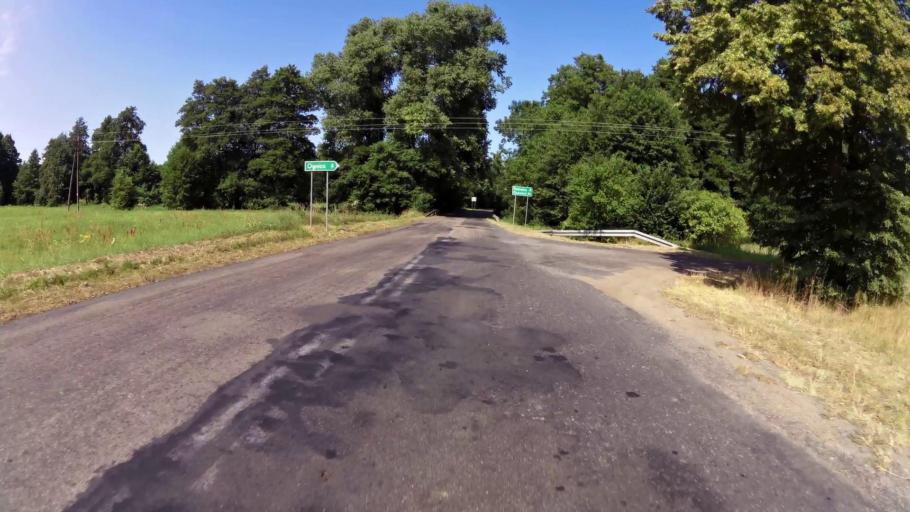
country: PL
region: West Pomeranian Voivodeship
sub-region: Powiat stargardzki
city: Dobrzany
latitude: 53.3343
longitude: 15.3930
